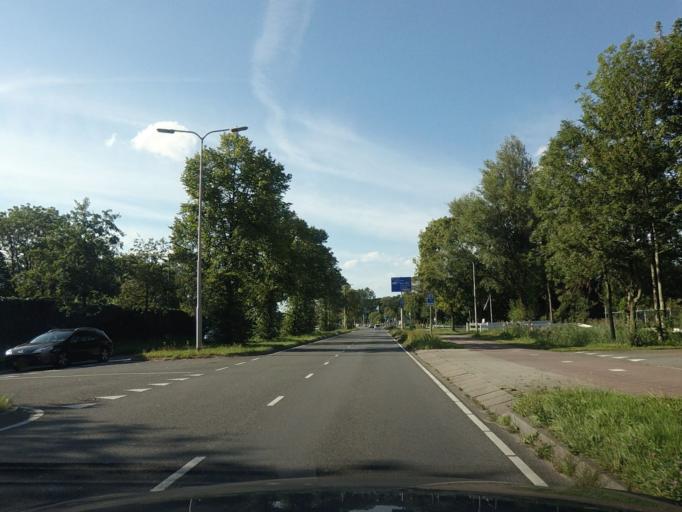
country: NL
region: South Holland
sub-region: Gemeente Leidschendam-Voorburg
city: Voorburg
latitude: 52.1035
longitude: 4.3618
